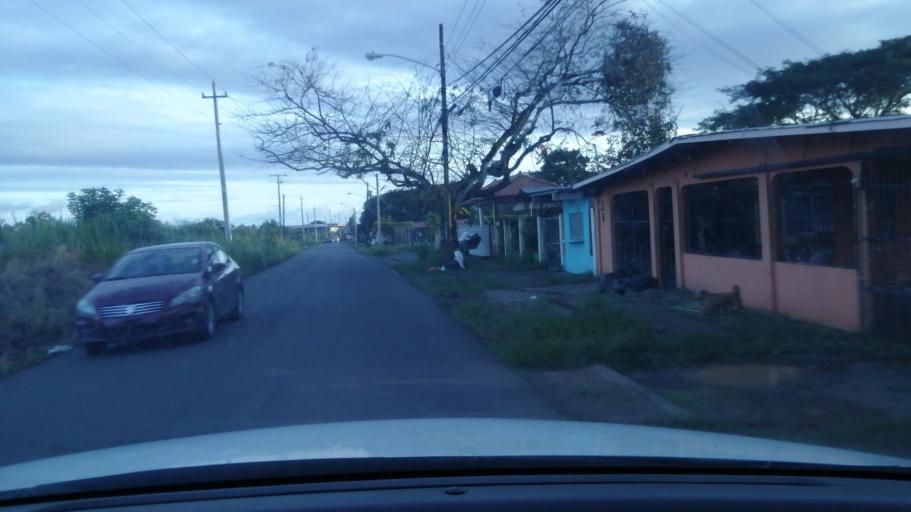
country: PA
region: Chiriqui
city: David
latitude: 8.4053
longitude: -82.4352
